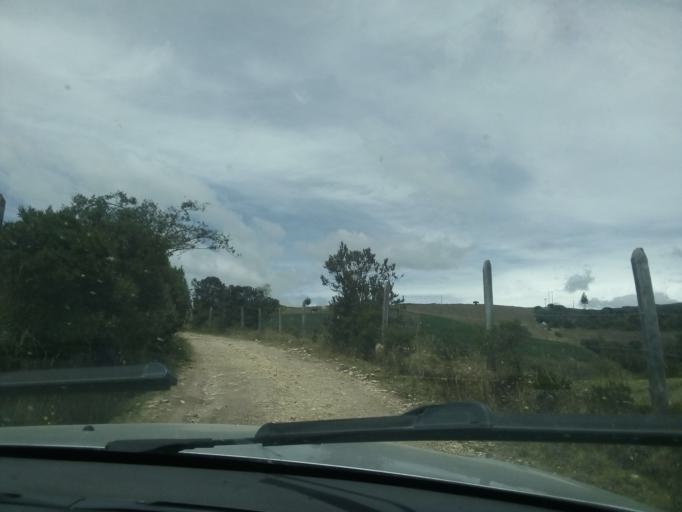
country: CO
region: Boyaca
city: Toca
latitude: 5.6169
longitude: -73.1188
